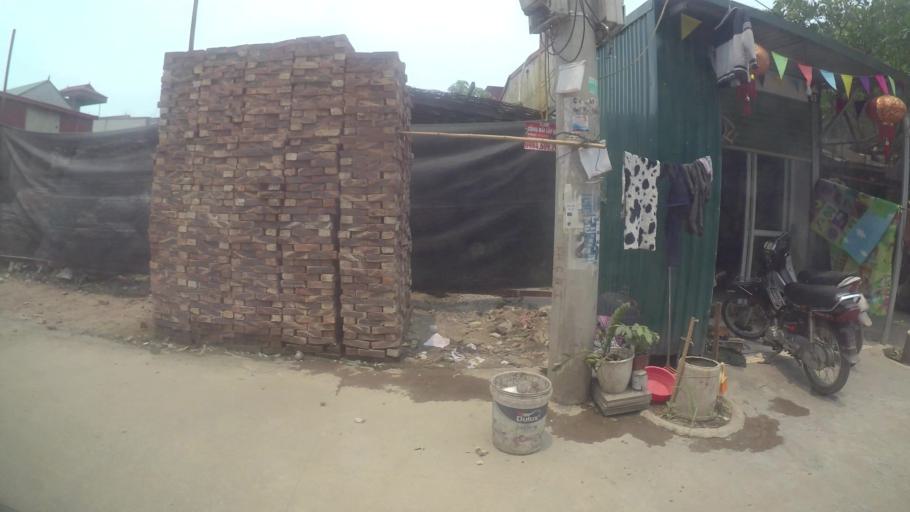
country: VN
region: Ha Noi
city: Ha Dong
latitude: 20.9922
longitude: 105.7403
